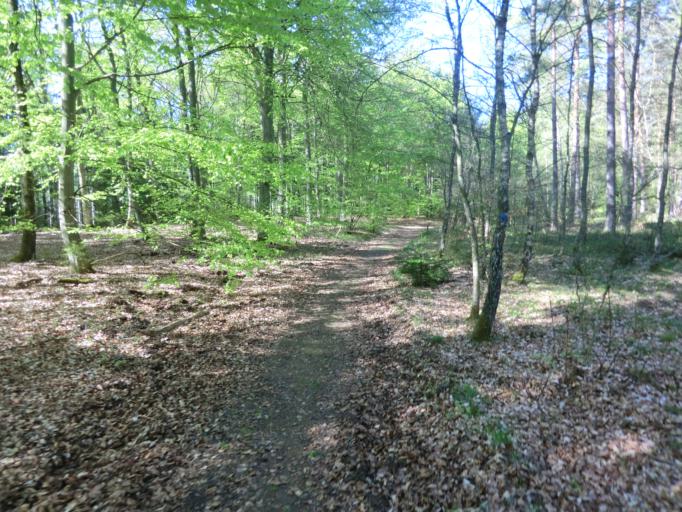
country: SE
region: Skane
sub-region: Sjobo Kommun
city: Sjoebo
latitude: 55.5729
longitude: 13.7146
